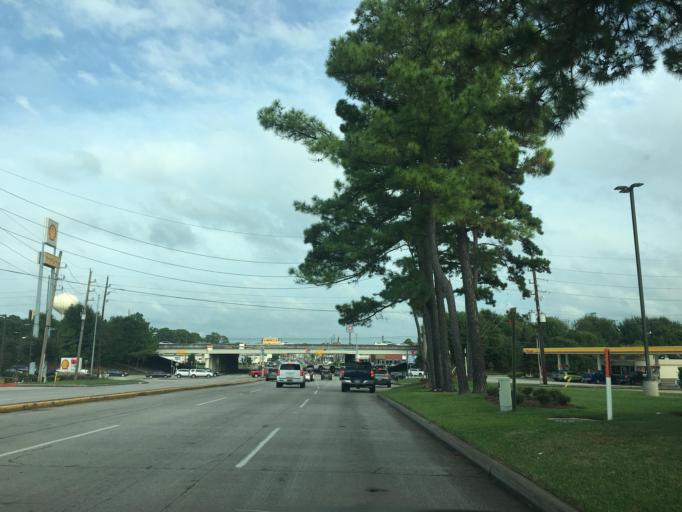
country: US
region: Texas
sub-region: Montgomery County
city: Oak Ridge North
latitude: 30.1266
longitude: -95.4451
